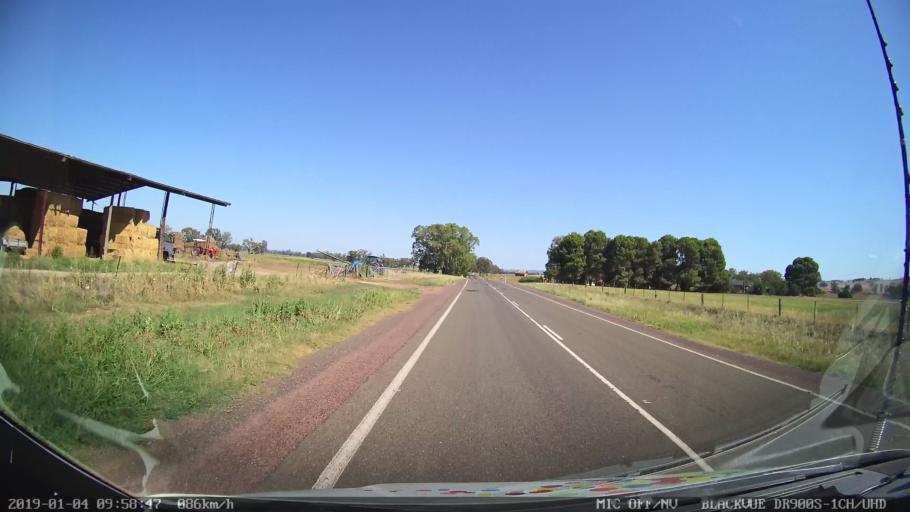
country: AU
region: New South Wales
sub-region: Cabonne
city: Canowindra
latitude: -33.5148
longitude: 148.3916
